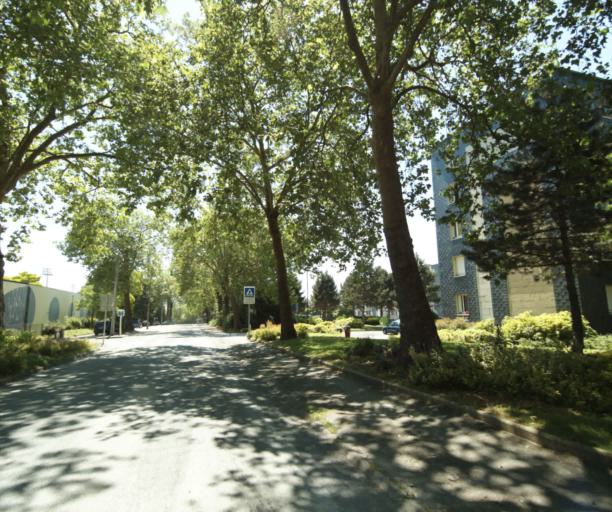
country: FR
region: Pays de la Loire
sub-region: Departement de la Mayenne
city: Laval
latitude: 48.0849
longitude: -0.7543
